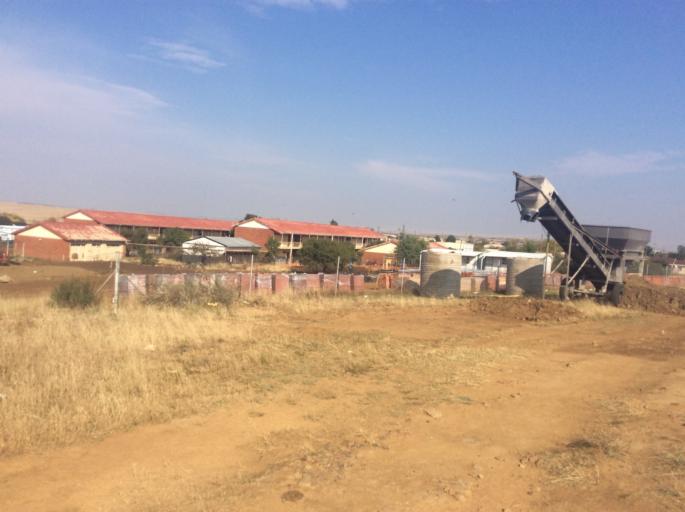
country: LS
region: Mafeteng
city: Mafeteng
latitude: -29.7216
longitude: 27.0135
